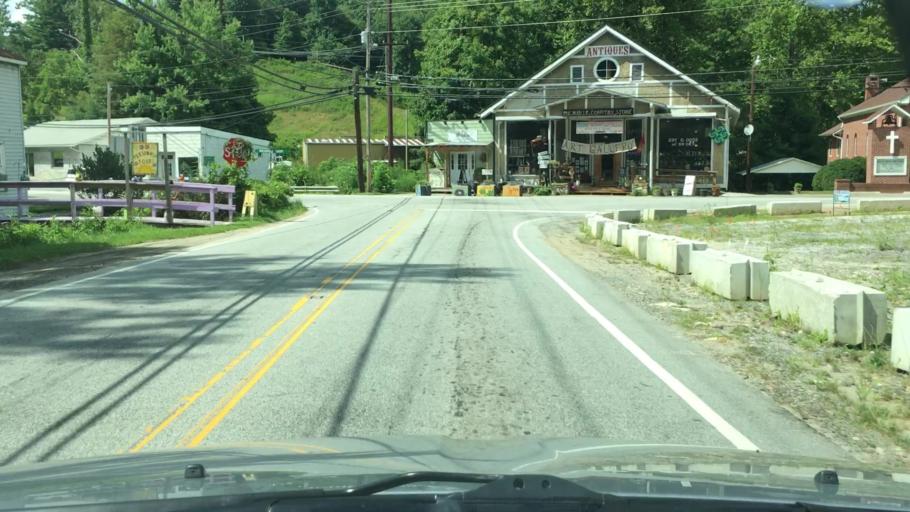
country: US
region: North Carolina
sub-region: Yancey County
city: Burnsville
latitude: 35.9072
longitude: -82.2157
